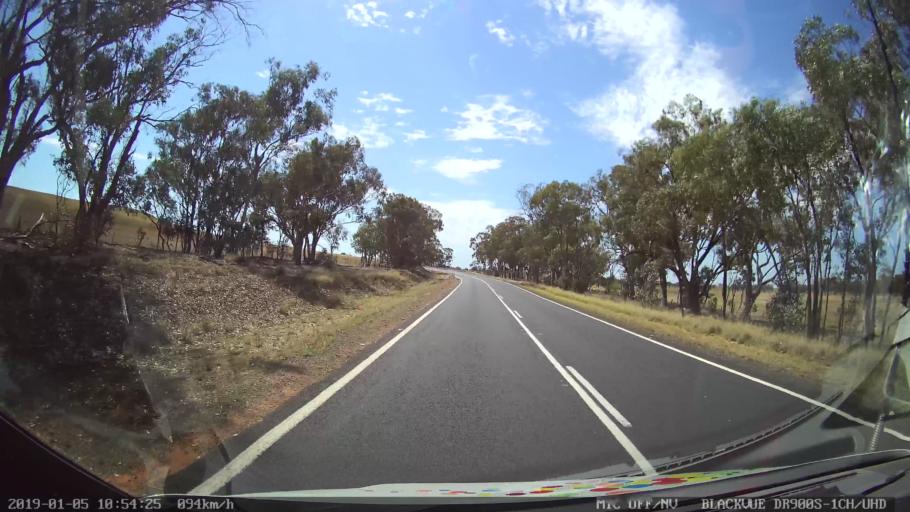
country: AU
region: New South Wales
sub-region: Warrumbungle Shire
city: Coonabarabran
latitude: -31.4500
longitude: 149.1277
